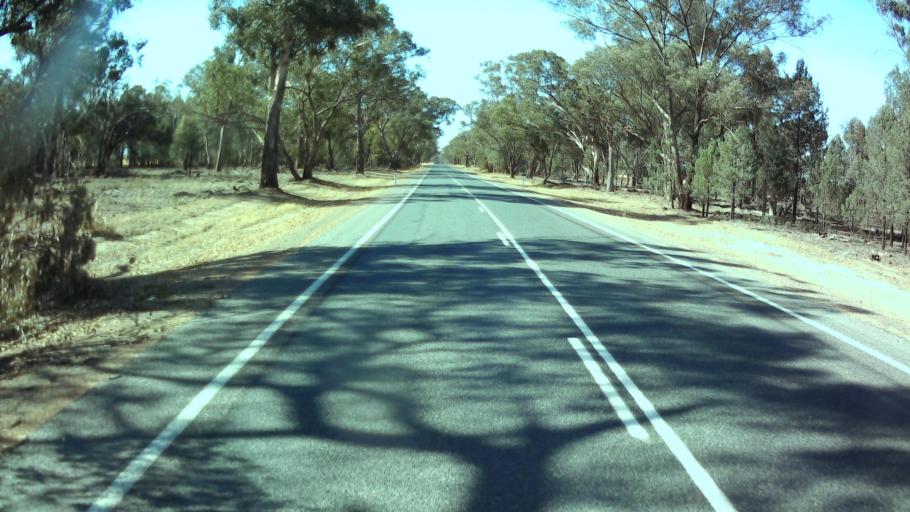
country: AU
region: New South Wales
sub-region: Weddin
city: Grenfell
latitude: -33.7435
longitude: 148.0886
